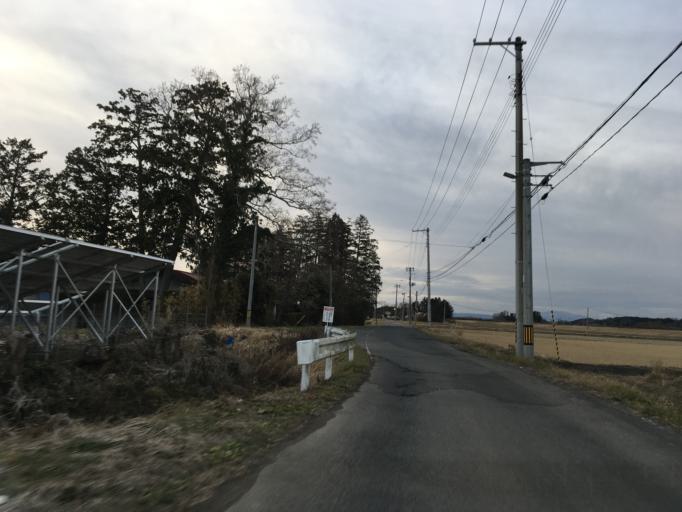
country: JP
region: Miyagi
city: Kogota
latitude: 38.6492
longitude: 141.0573
